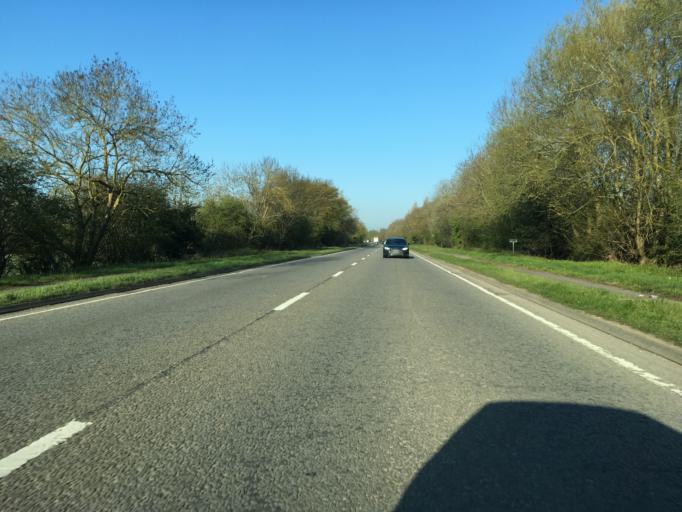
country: GB
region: England
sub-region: Oxfordshire
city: Yarnton
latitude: 51.7931
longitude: -1.3103
